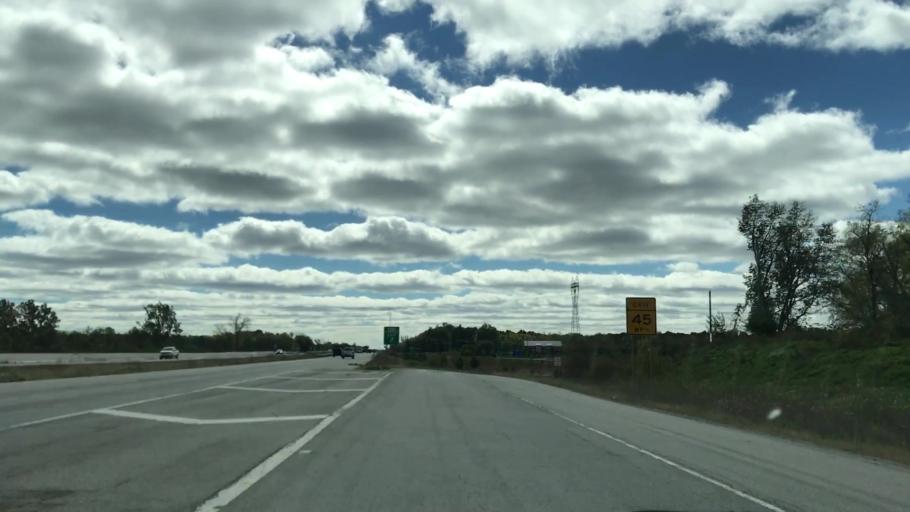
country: US
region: Indiana
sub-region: Hamilton County
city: Westfield
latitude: 40.0976
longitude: -86.1282
